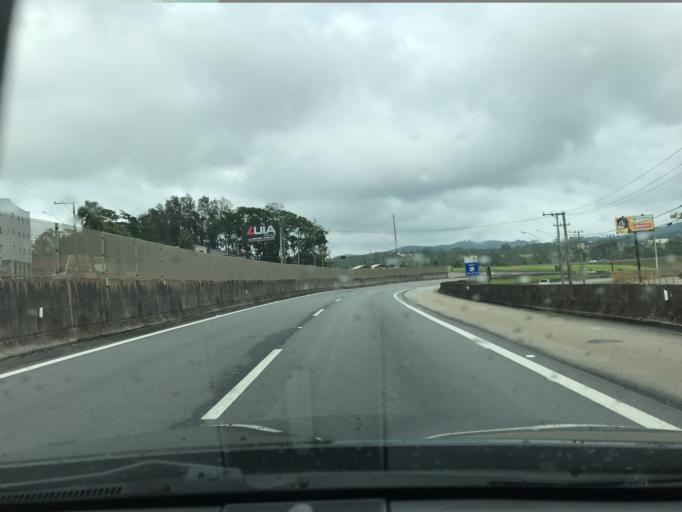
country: BR
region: Sao Paulo
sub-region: Vargem Grande Paulista
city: Vargem Grande Paulista
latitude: -23.6061
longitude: -47.0300
